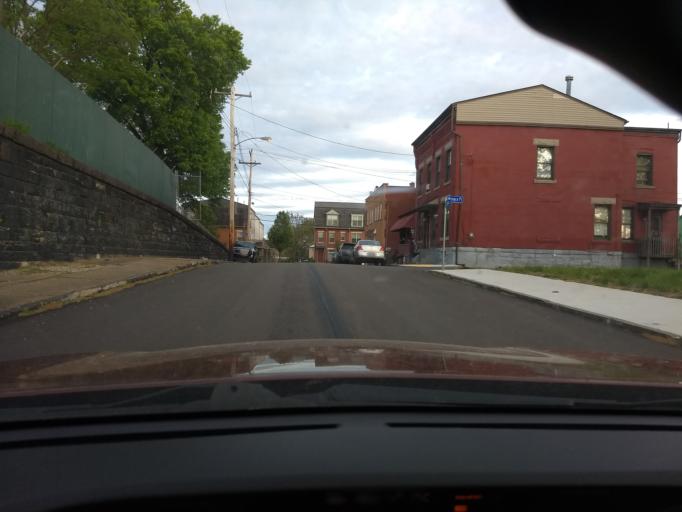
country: US
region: Pennsylvania
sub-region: Allegheny County
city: Pittsburgh
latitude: 40.4469
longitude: -79.9831
